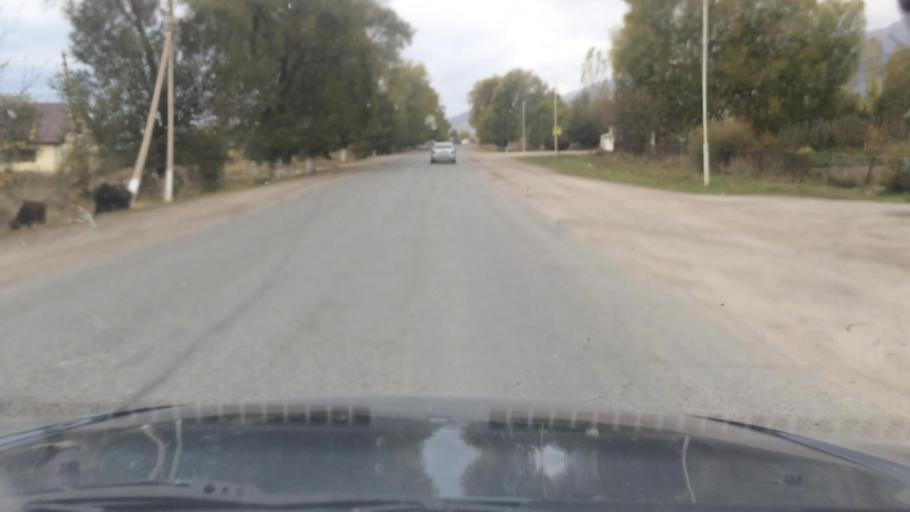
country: KG
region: Ysyk-Koel
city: Tyup
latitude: 42.7857
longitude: 78.2518
